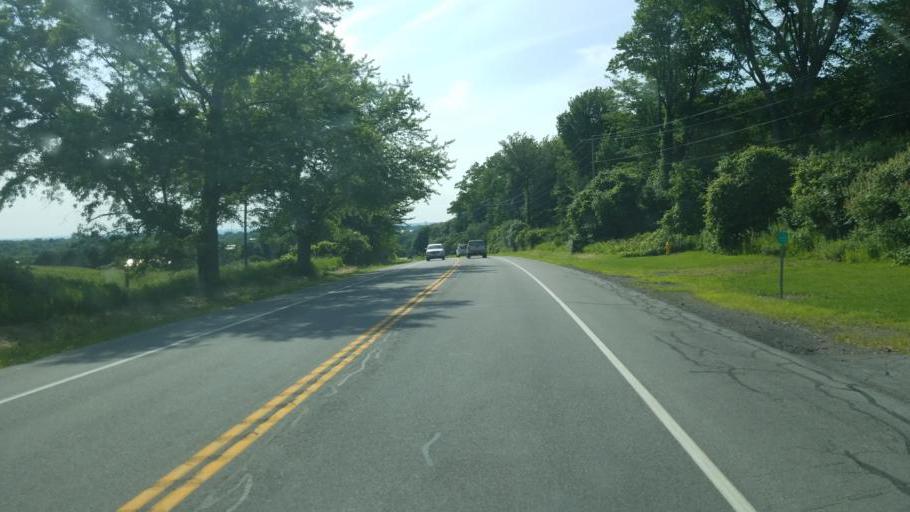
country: US
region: New York
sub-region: Livingston County
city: Lima
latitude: 42.9036
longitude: -77.6583
